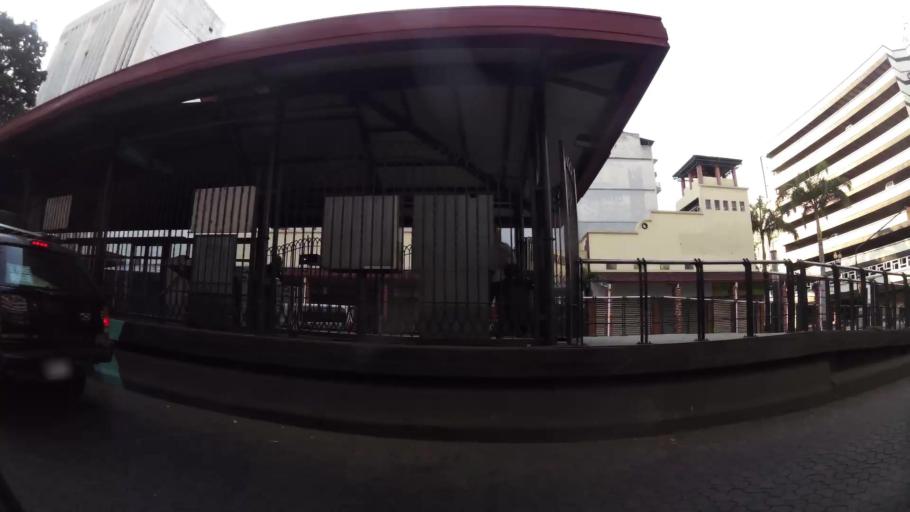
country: EC
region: Guayas
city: Guayaquil
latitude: -2.1945
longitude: -79.8819
